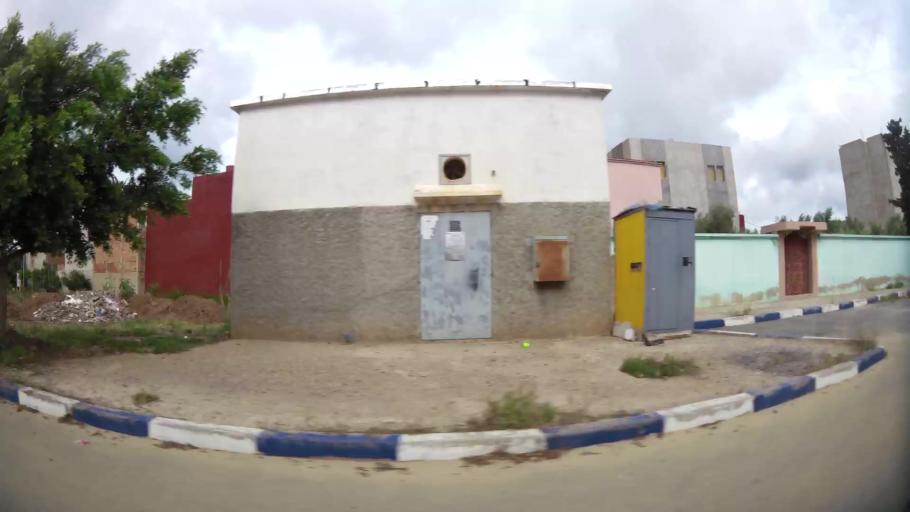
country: MA
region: Oriental
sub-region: Nador
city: Nador
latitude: 35.1587
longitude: -2.9183
